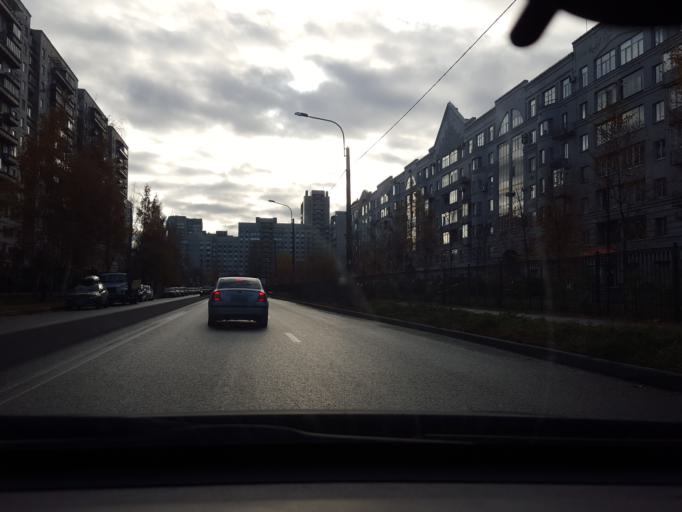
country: RU
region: St.-Petersburg
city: Ozerki
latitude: 60.0468
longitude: 30.3188
